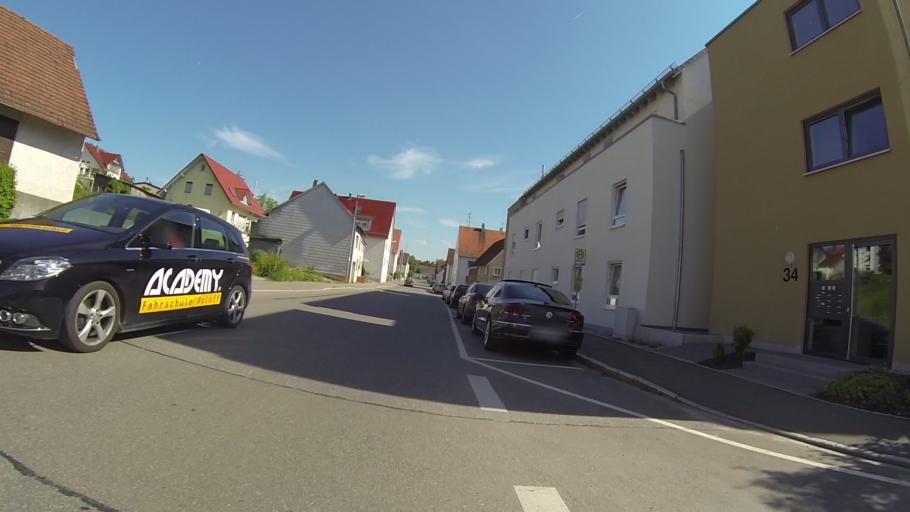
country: DE
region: Baden-Wuerttemberg
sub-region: Tuebingen Region
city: Laupheim
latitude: 48.2264
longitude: 9.8859
